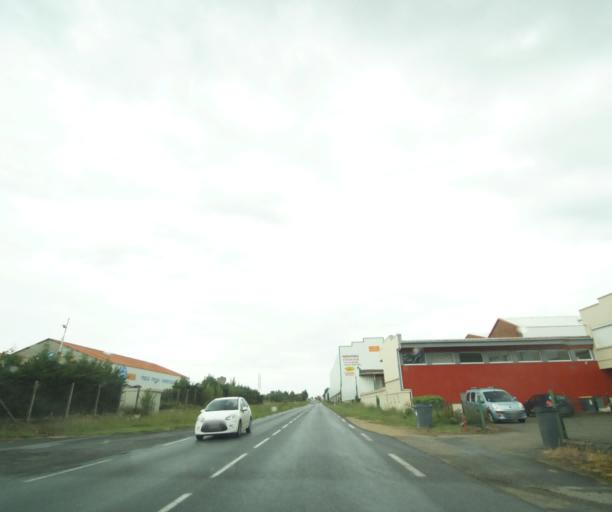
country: FR
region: Poitou-Charentes
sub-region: Departement des Deux-Sevres
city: Chatillon-sur-Thouet
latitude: 46.6687
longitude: -0.2465
